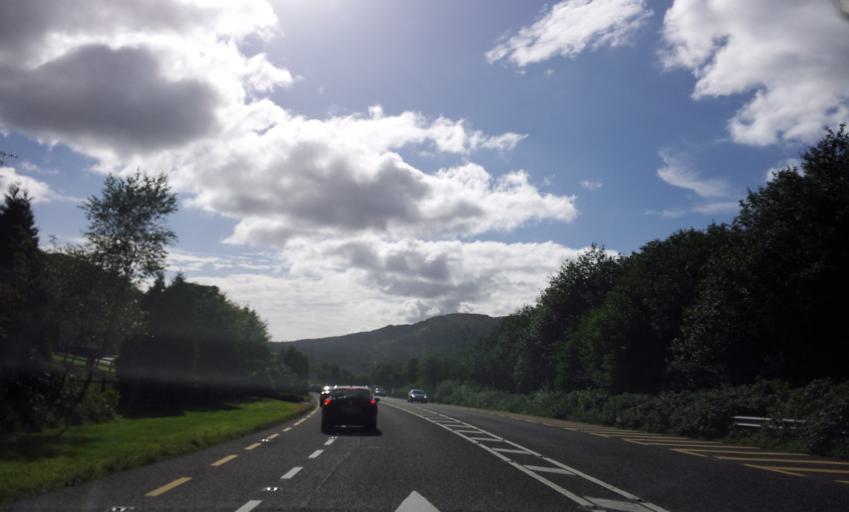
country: IE
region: Munster
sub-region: Ciarrai
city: Cill Airne
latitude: 51.9825
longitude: -9.3117
